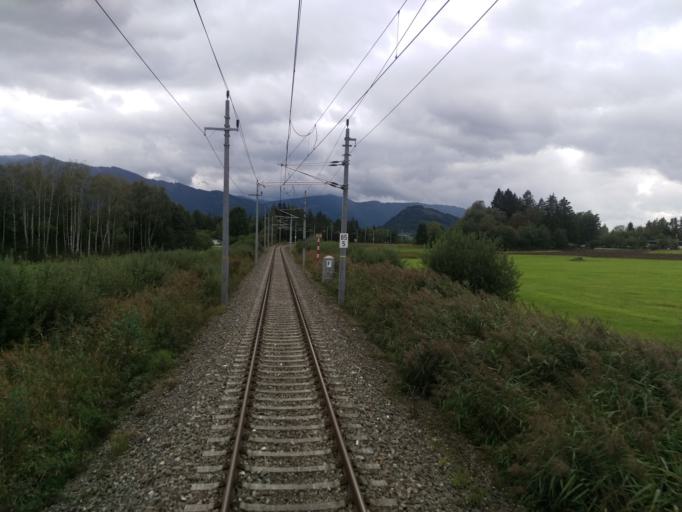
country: AT
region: Styria
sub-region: Politischer Bezirk Liezen
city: Worschach
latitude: 47.5521
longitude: 14.1589
